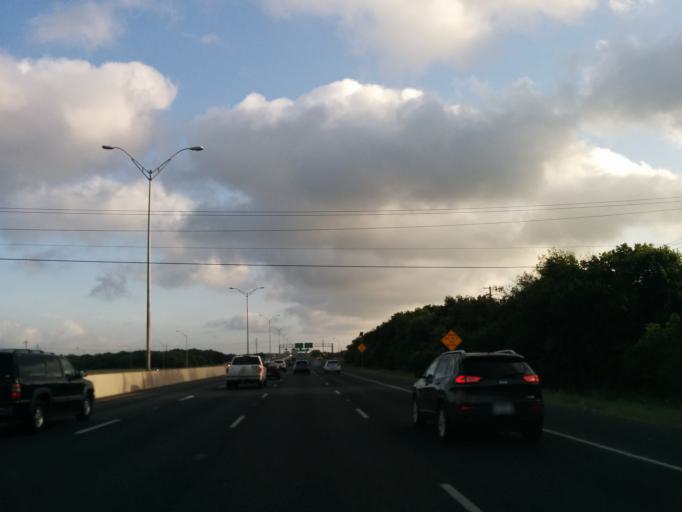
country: US
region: Texas
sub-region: Bexar County
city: Olmos Park
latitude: 29.4848
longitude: -98.4822
